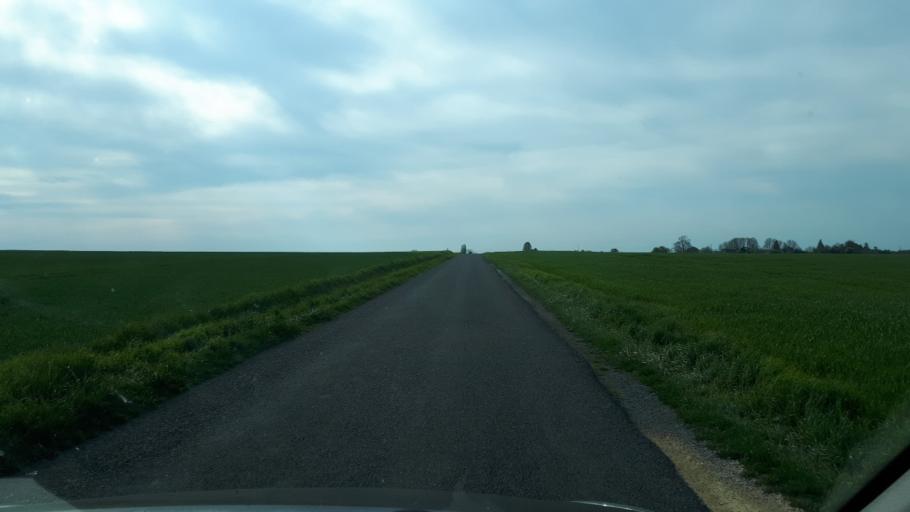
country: FR
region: Centre
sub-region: Departement du Cher
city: Sancerre
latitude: 47.2948
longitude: 2.7518
